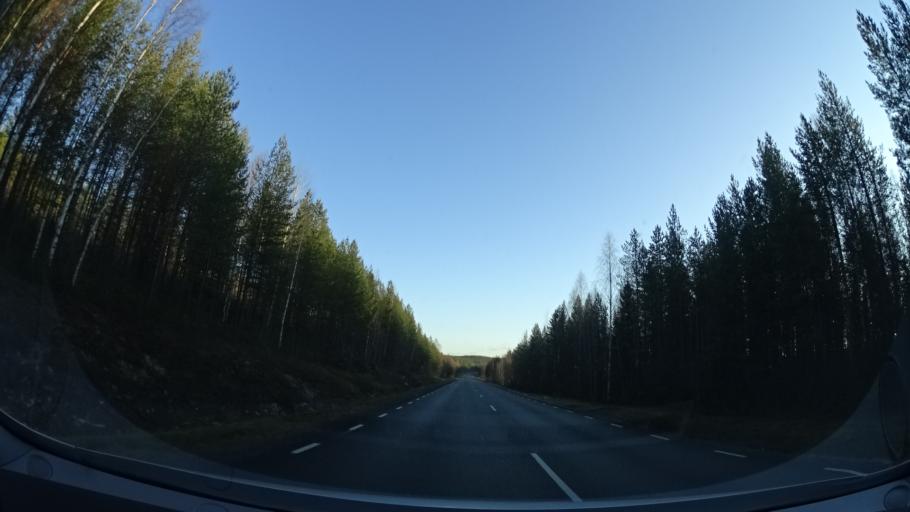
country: SE
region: Vaesterbotten
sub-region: Lycksele Kommun
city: Lycksele
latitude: 64.6420
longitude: 18.6686
